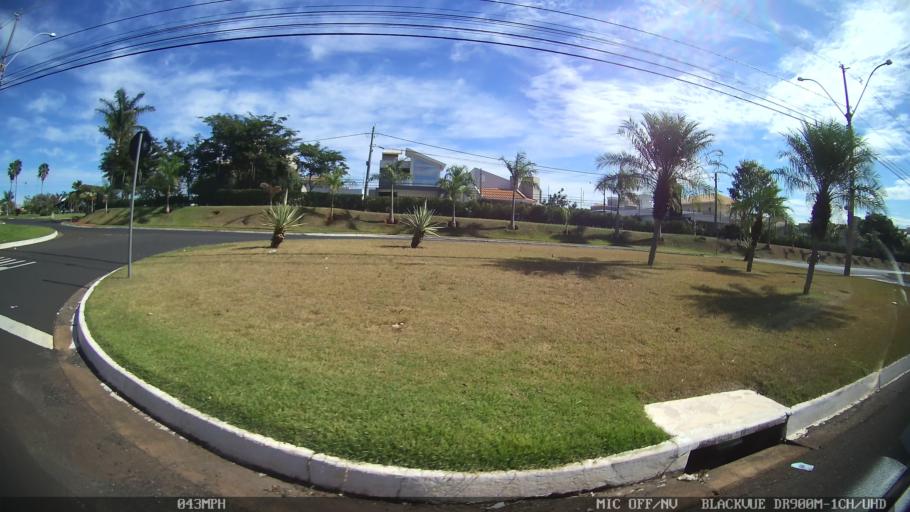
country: BR
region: Sao Paulo
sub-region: Sao Jose Do Rio Preto
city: Sao Jose do Rio Preto
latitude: -20.8212
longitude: -49.4815
